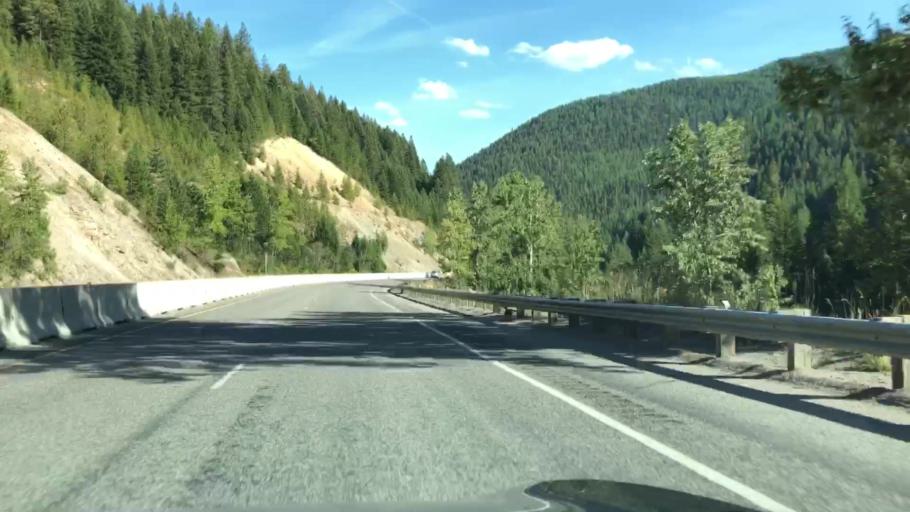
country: US
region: Montana
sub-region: Sanders County
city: Thompson Falls
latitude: 47.3985
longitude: -115.4592
